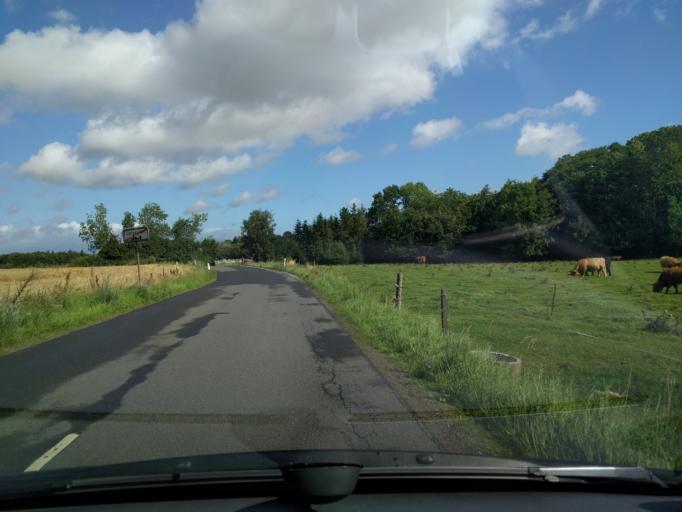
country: DK
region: South Denmark
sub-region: Kerteminde Kommune
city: Langeskov
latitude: 55.3661
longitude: 10.5873
